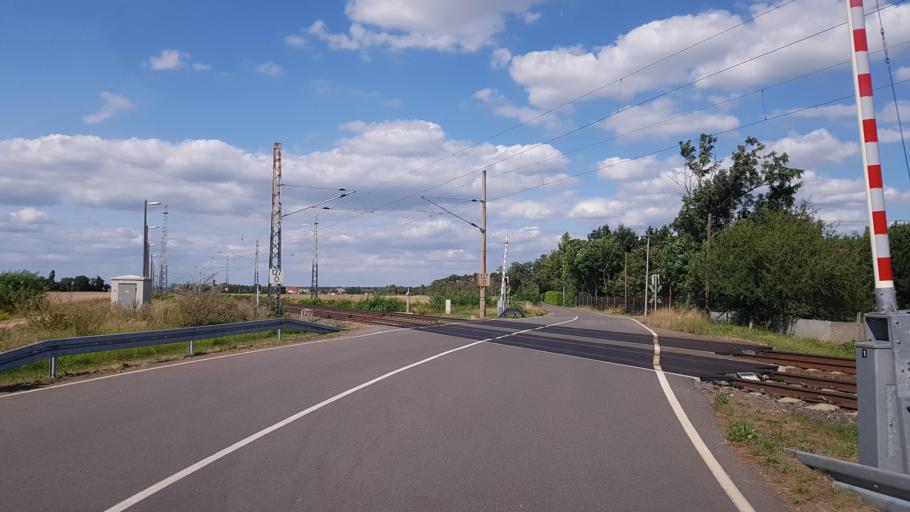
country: DE
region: Brandenburg
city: Muhlberg
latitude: 51.4546
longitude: 13.2986
